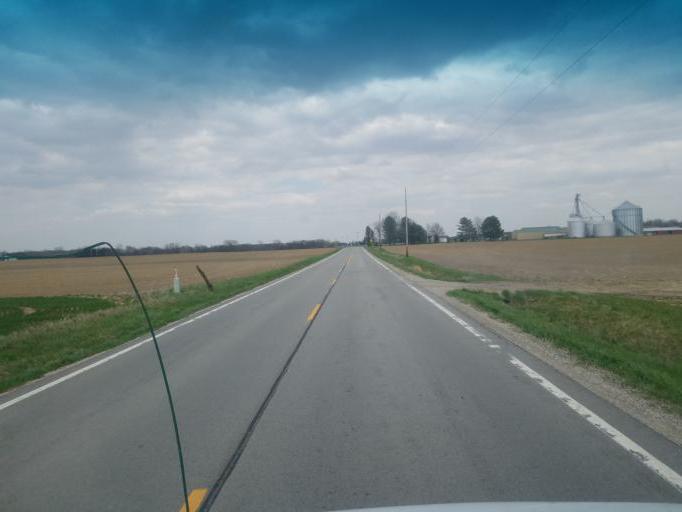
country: US
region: Ohio
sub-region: Crawford County
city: Bucyrus
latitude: 40.9501
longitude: -83.0793
